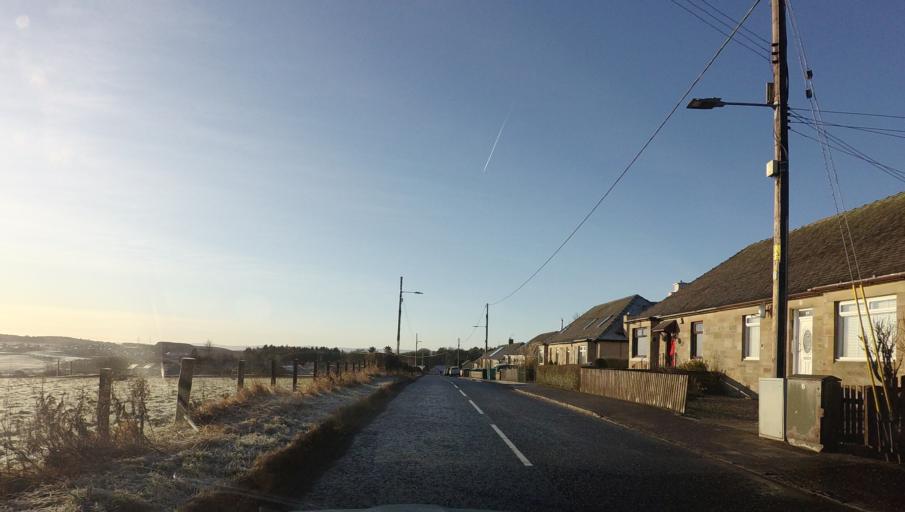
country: GB
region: Scotland
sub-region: North Lanarkshire
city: Shotts
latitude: 55.8133
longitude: -3.8358
